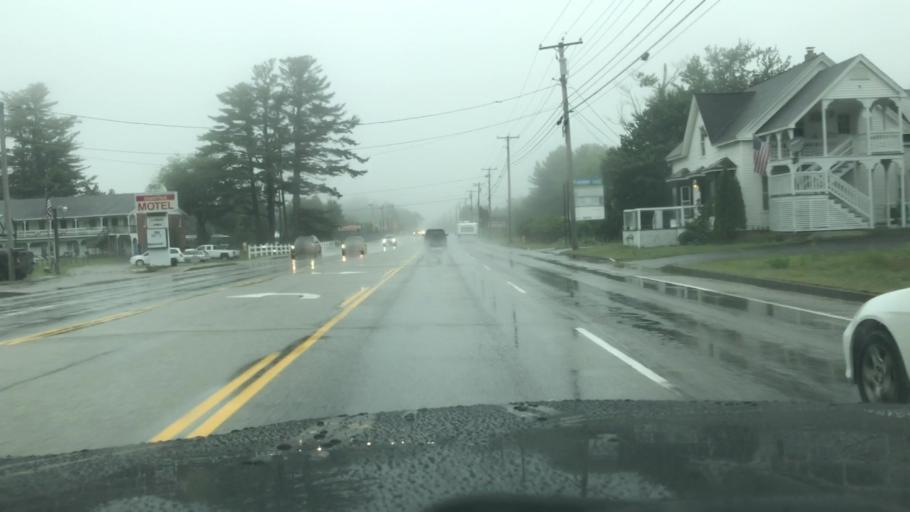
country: US
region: Maine
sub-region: Cumberland County
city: West Scarborough
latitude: 43.5494
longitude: -70.4095
